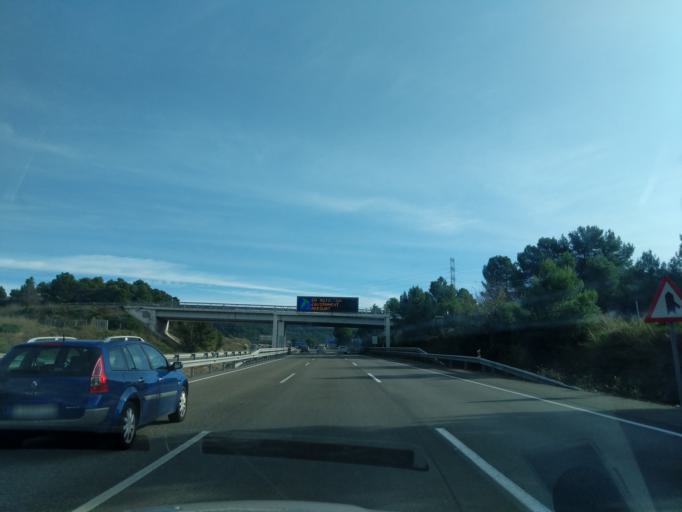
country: ES
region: Catalonia
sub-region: Provincia de Barcelona
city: Castelloli
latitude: 41.5981
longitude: 1.7100
